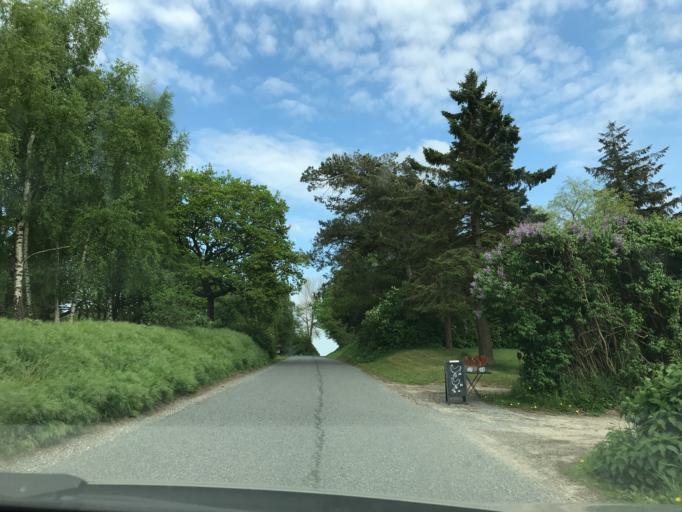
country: DK
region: South Denmark
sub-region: Assens Kommune
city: Assens
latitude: 55.3248
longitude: 9.9128
